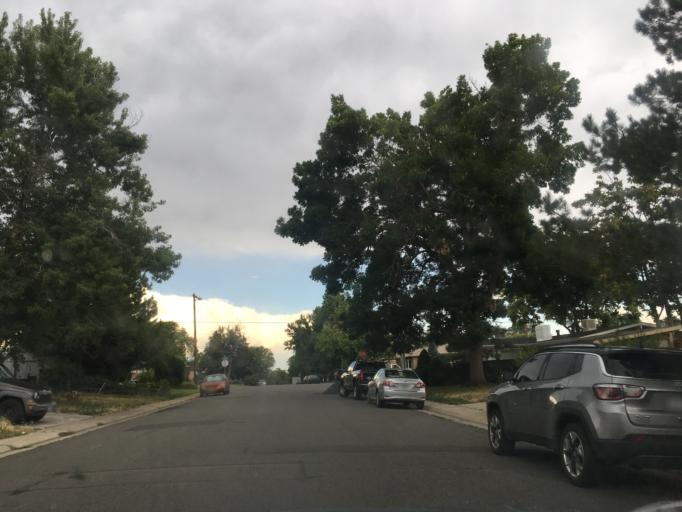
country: US
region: Colorado
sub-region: Arapahoe County
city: Sheridan
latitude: 39.6742
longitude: -105.0369
